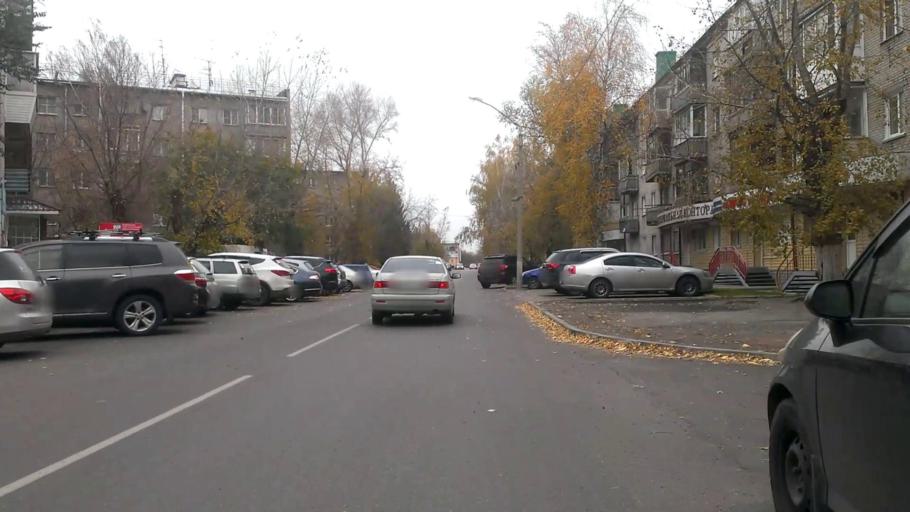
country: RU
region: Altai Krai
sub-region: Gorod Barnaulskiy
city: Barnaul
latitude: 53.3497
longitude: 83.7710
